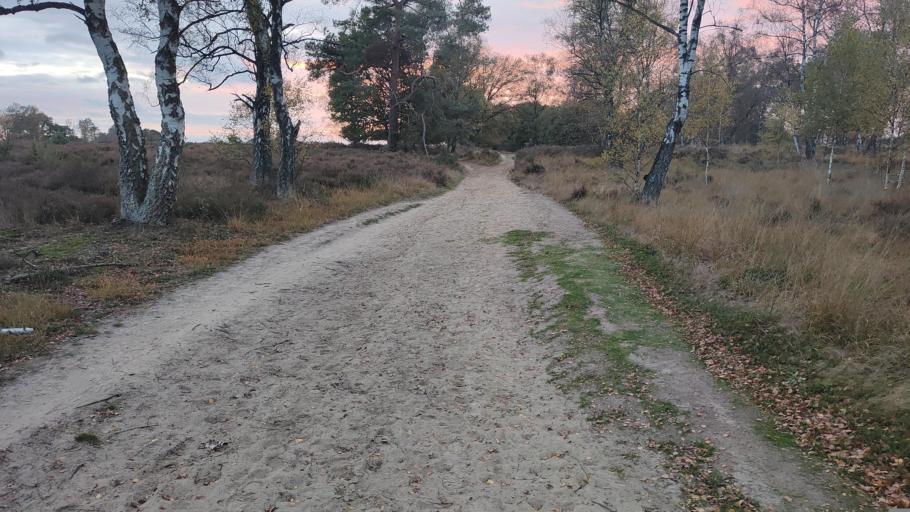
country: NL
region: Limburg
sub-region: Gemeente Roerdalen
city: Herkenbosch
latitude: 51.1695
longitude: 6.0979
